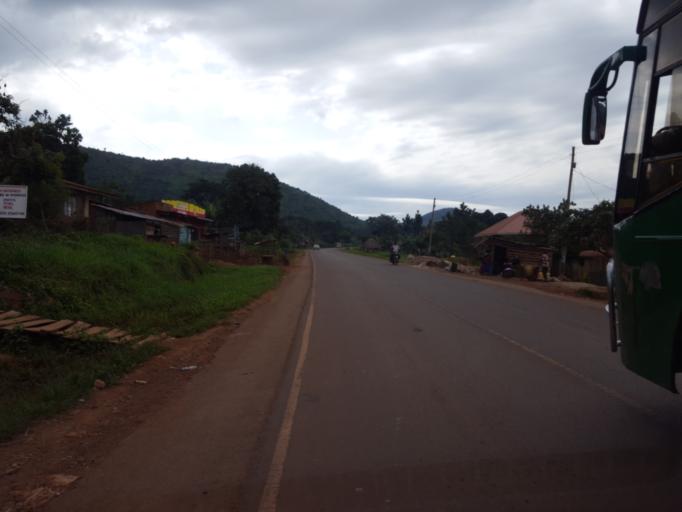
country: UG
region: Central Region
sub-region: Mityana District
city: Mityana
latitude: 0.6708
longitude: 32.0755
